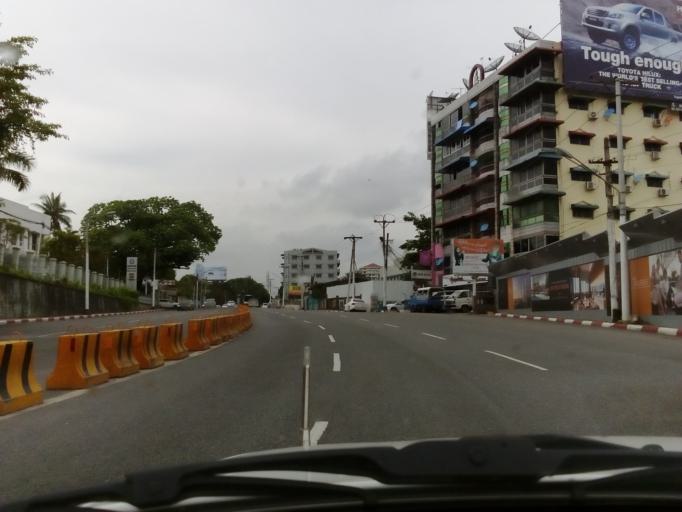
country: MM
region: Yangon
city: Yangon
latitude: 16.8107
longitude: 96.1562
